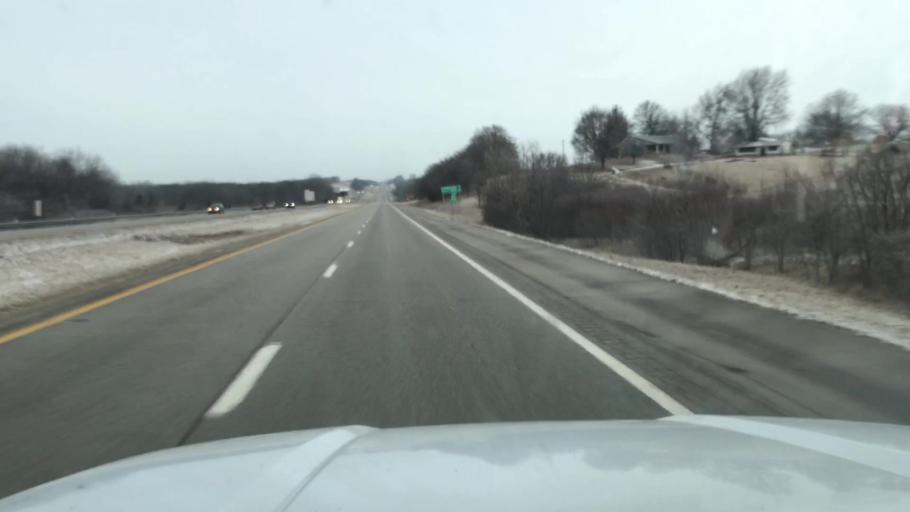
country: US
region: Missouri
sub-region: Andrew County
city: Country Club Village
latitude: 39.8656
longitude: -94.8226
